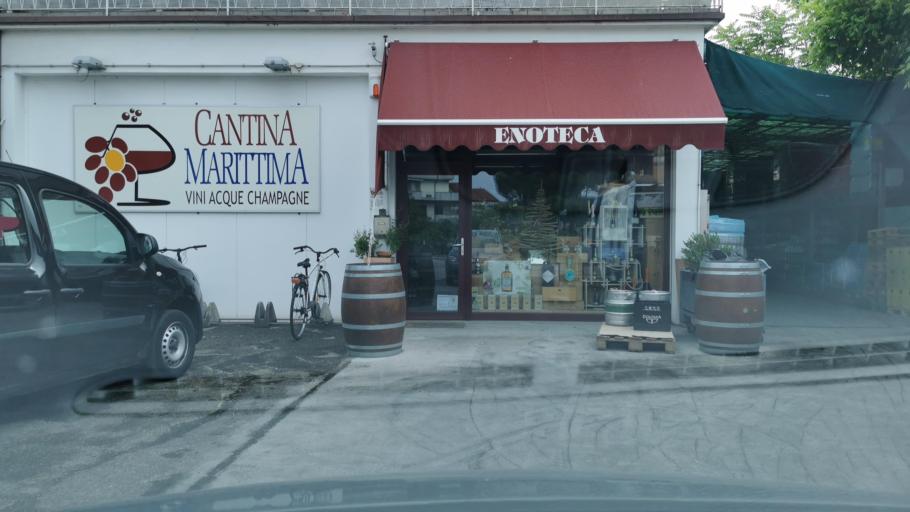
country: IT
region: Emilia-Romagna
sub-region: Provincia di Ravenna
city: Cervia
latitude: 44.2663
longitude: 12.3461
